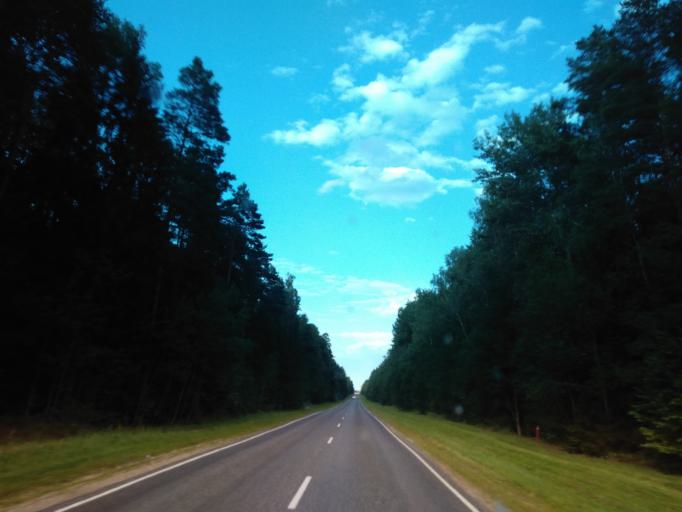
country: BY
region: Minsk
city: Uzda
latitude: 53.4286
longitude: 27.4563
